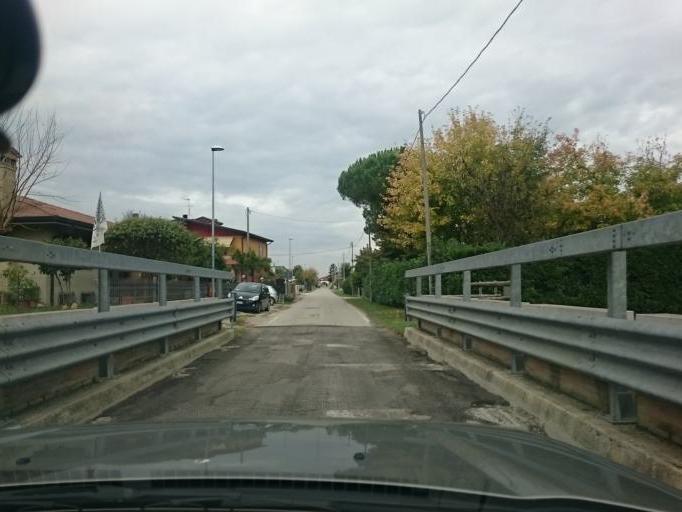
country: IT
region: Veneto
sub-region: Provincia di Padova
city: Vallonga
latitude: 45.2660
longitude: 12.0709
